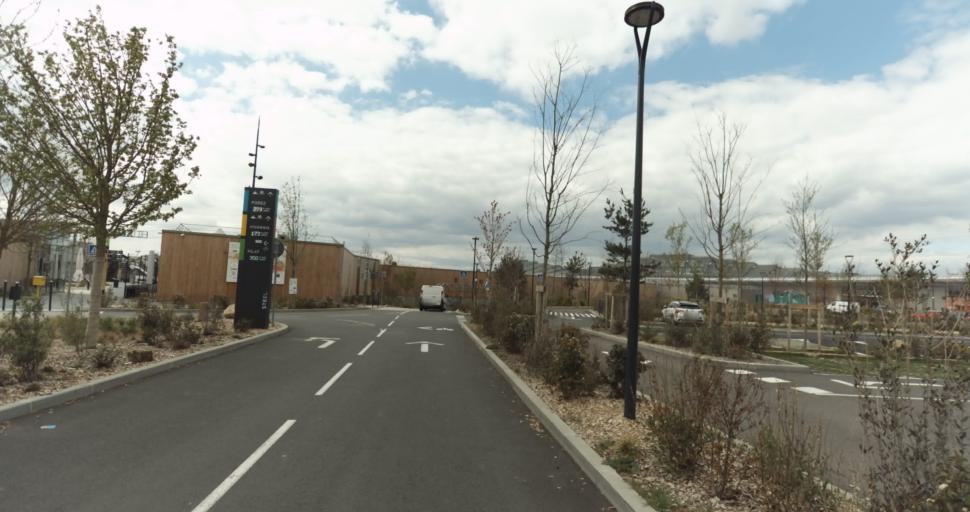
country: FR
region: Rhone-Alpes
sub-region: Departement de la Loire
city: Saint-Jean-Bonnefonds
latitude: 45.4463
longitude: 4.4224
